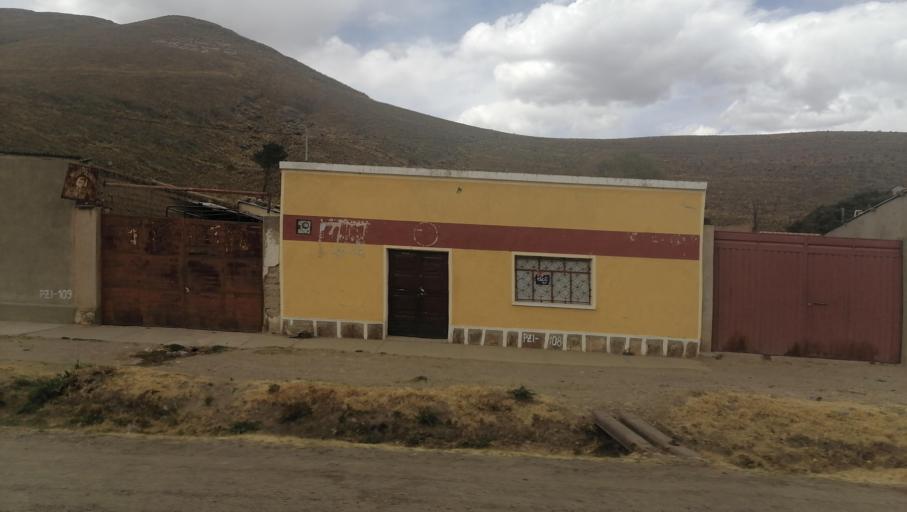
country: BO
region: Oruro
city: Totoral
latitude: -18.5947
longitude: -66.9229
